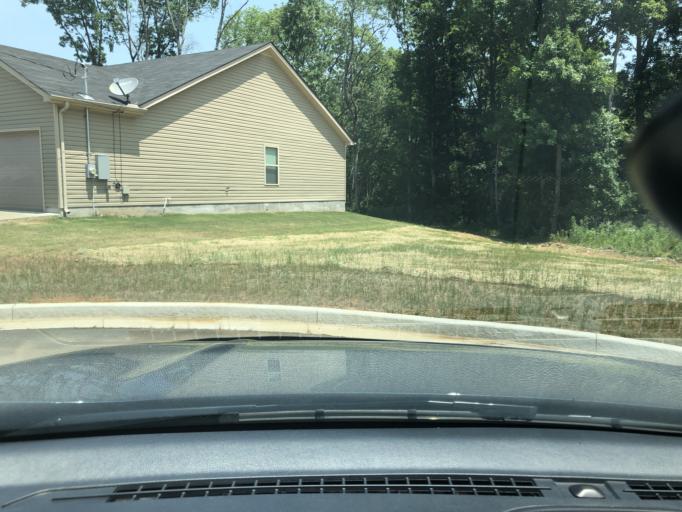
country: US
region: Tennessee
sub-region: Rutherford County
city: La Vergne
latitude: 36.0555
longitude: -86.6098
